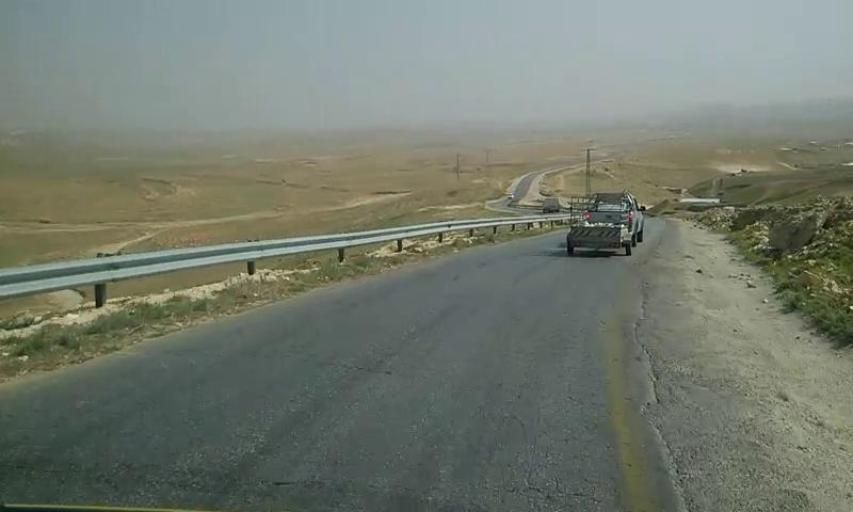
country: PS
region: West Bank
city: An Nuway`imah
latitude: 31.9187
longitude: 35.3885
